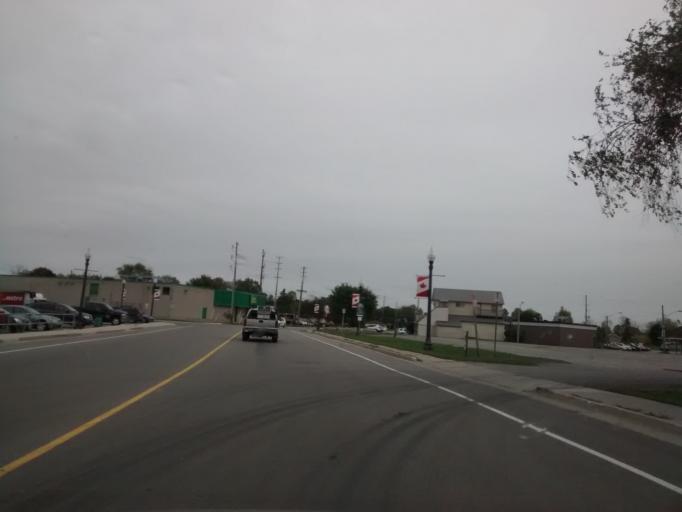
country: CA
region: Ontario
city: Welland
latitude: 42.9013
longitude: -79.6176
